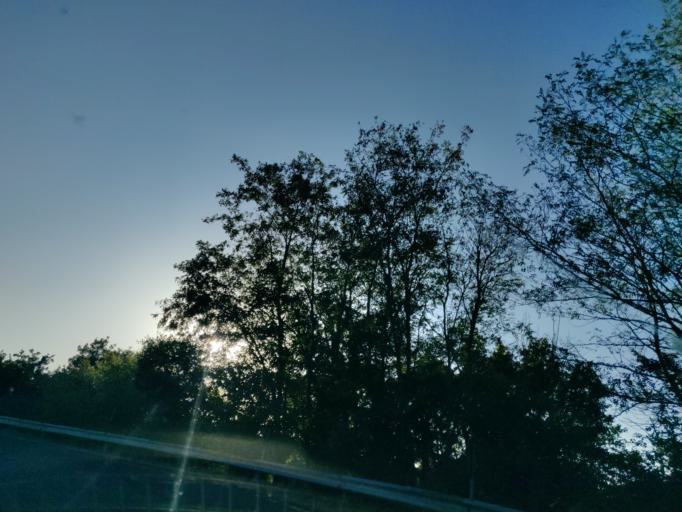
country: IT
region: Latium
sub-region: Provincia di Viterbo
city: Latera
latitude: 42.6395
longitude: 11.8383
